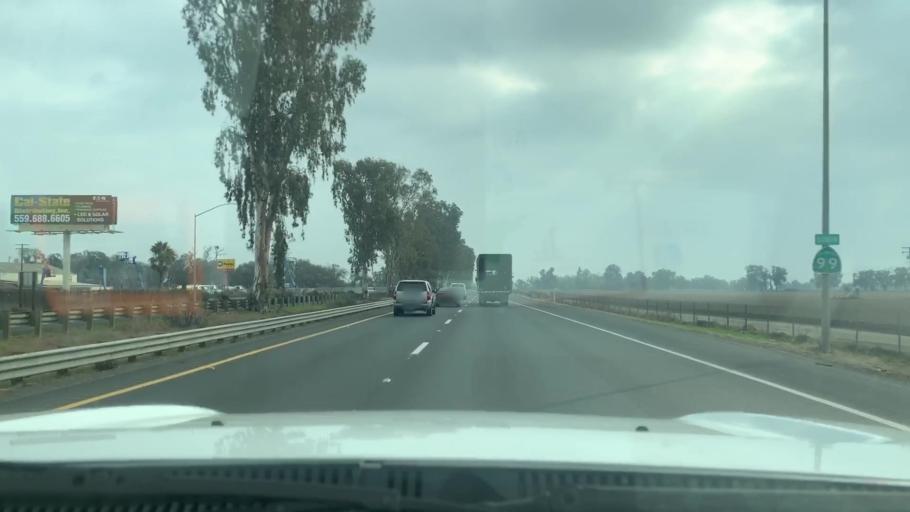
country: US
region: California
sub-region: Tulare County
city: Tulare
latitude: 36.1503
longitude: -119.3309
